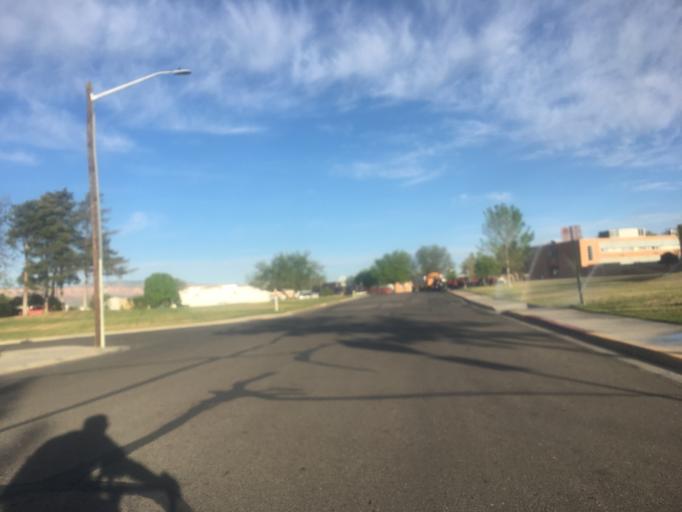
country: US
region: Colorado
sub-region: Mesa County
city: Grand Junction
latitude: 39.0785
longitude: -108.5624
